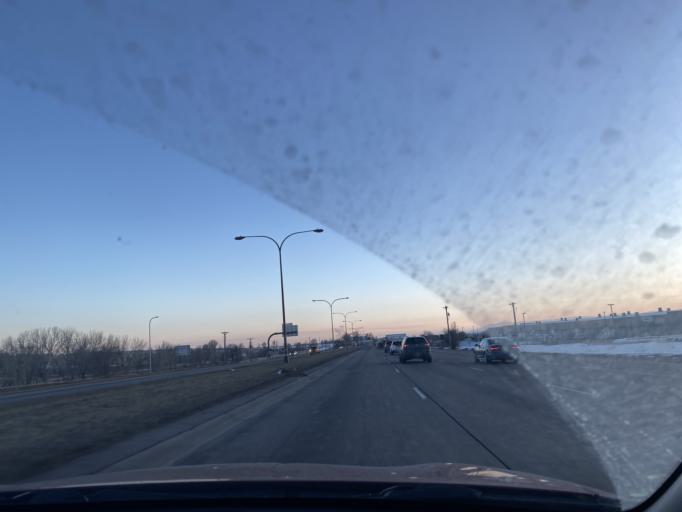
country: US
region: Colorado
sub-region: El Paso County
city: Cimarron Hills
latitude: 38.8367
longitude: -104.7209
